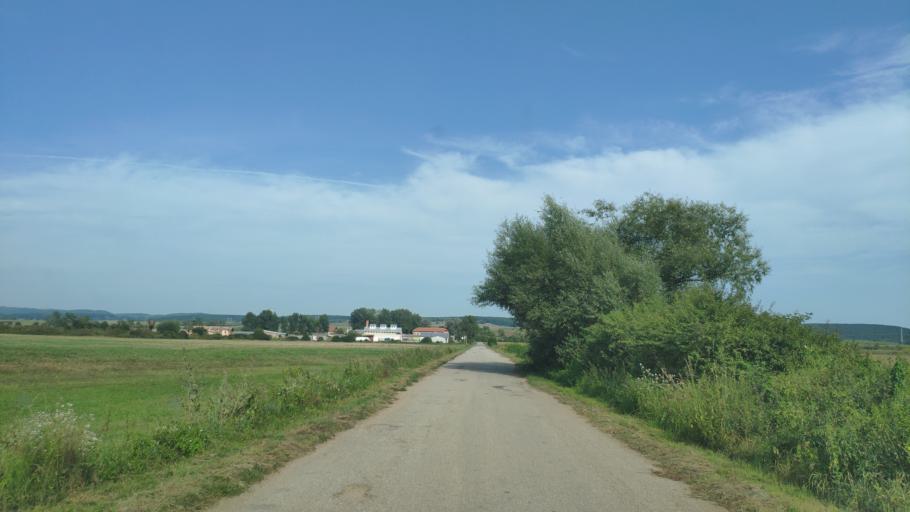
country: HU
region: Borsod-Abauj-Zemplen
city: Putnok
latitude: 48.4541
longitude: 20.3352
